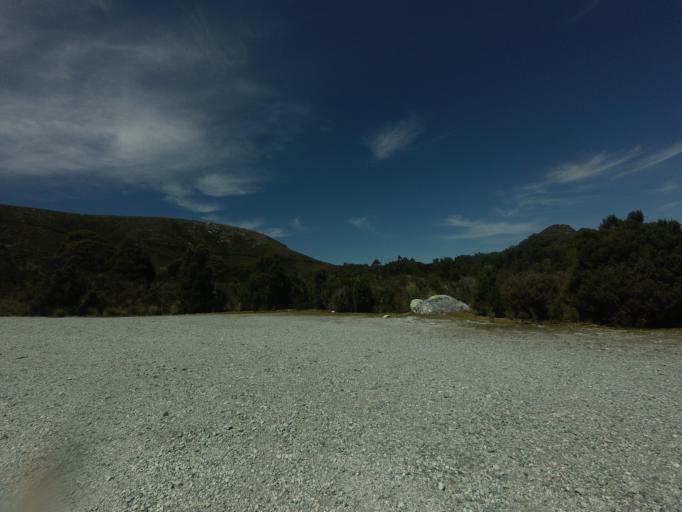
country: AU
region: Tasmania
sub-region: West Coast
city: Queenstown
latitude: -42.7871
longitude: 146.0606
